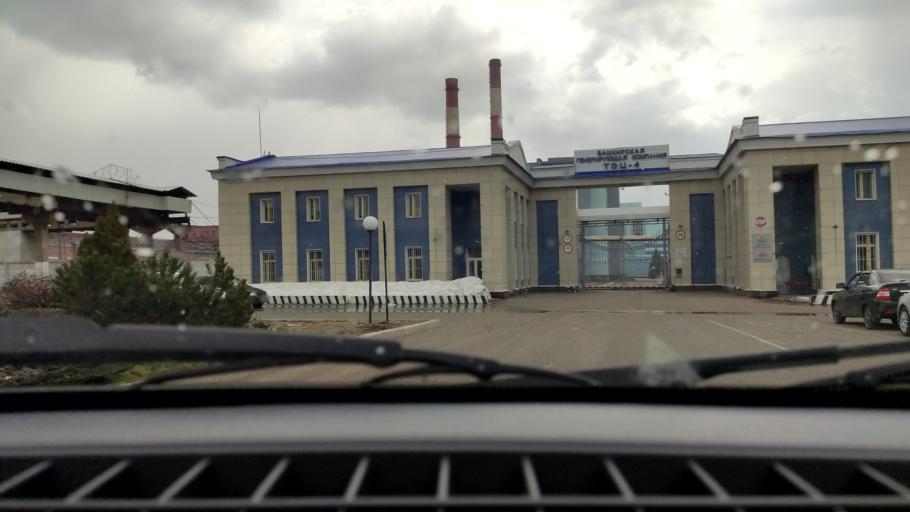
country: RU
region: Bashkortostan
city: Blagoveshchensk
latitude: 54.9176
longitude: 56.0699
